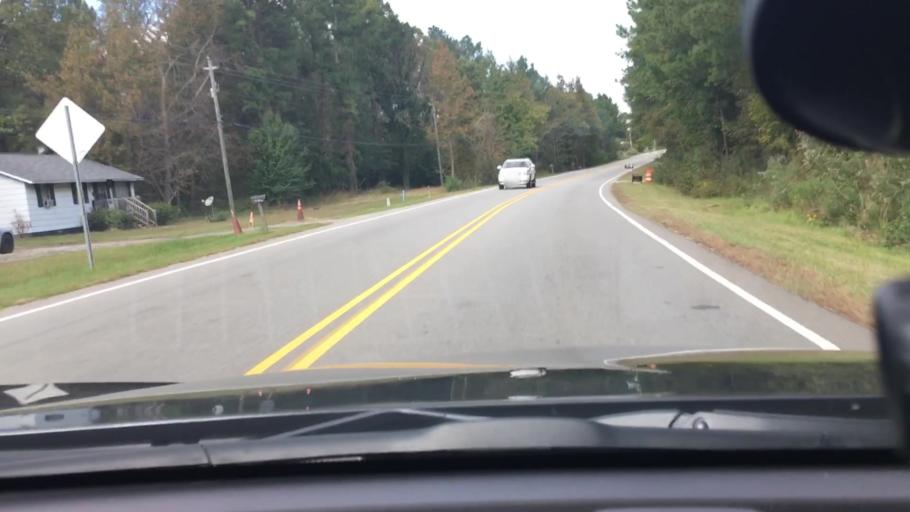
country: US
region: North Carolina
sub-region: Wake County
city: Holly Springs
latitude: 35.6850
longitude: -78.8340
